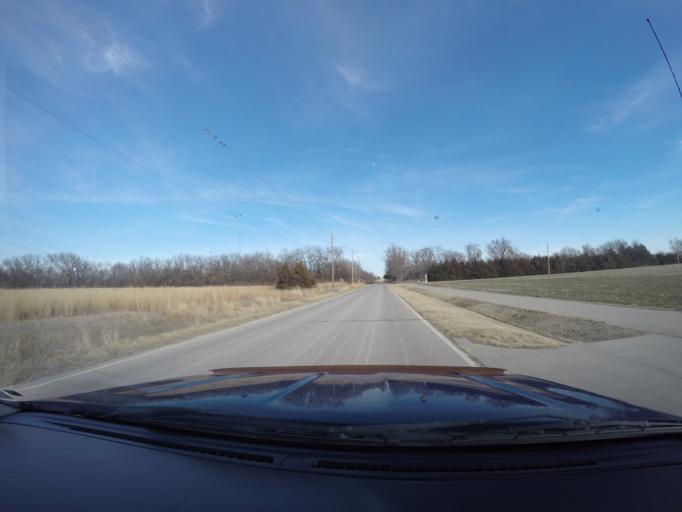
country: US
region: Kansas
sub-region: Harvey County
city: North Newton
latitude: 38.0718
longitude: -97.3380
